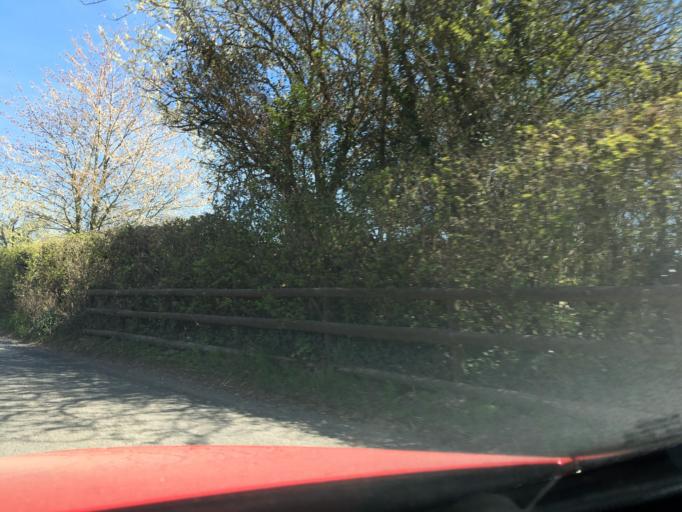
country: GB
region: Wales
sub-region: Monmouthshire
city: Llangwm
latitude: 51.7183
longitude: -2.8428
